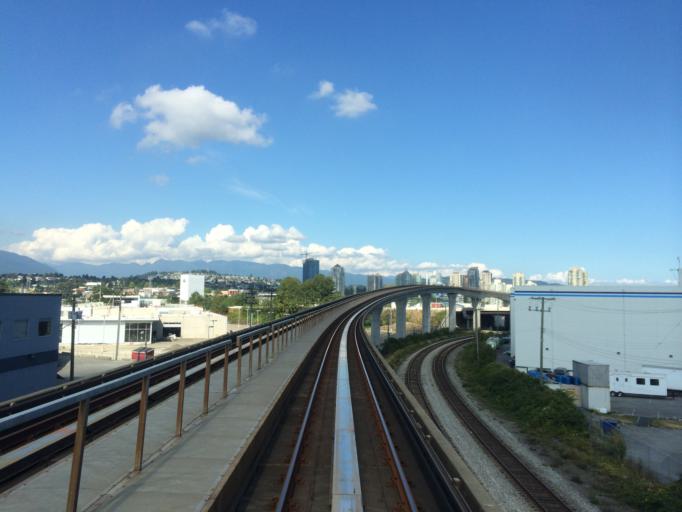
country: CA
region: British Columbia
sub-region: Fraser Valley Regional District
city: North Vancouver
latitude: 49.2618
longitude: -123.0296
